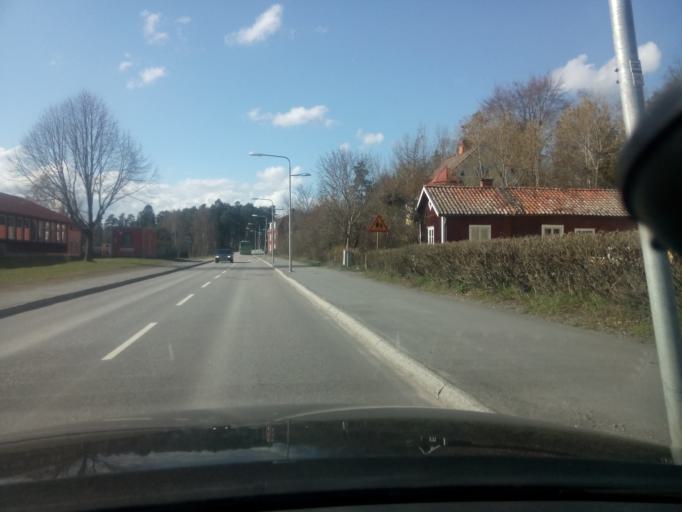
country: SE
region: Soedermanland
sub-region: Flens Kommun
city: Malmkoping
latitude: 59.1371
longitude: 16.7218
